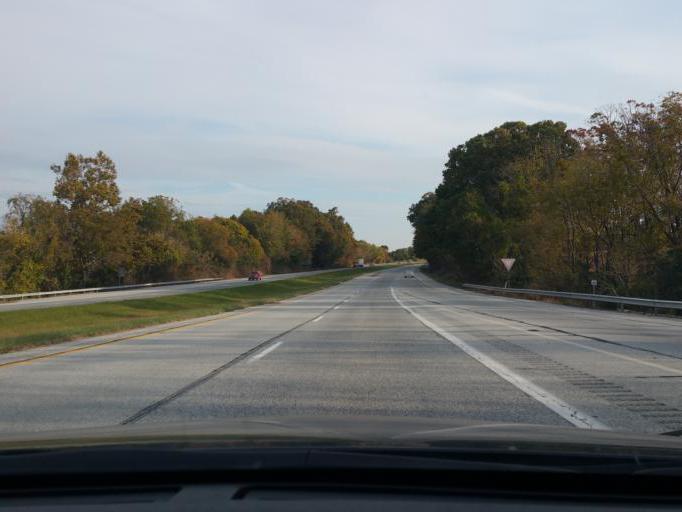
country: US
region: Pennsylvania
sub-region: Chester County
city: Oxford
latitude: 39.7535
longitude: -76.0232
